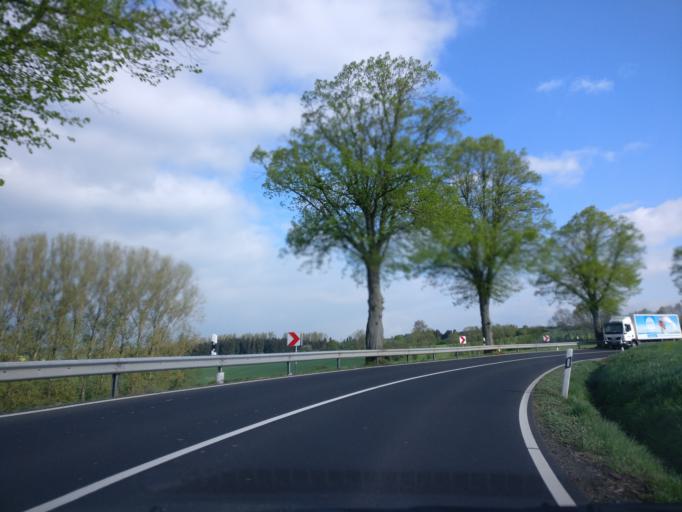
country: DE
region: Lower Saxony
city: Scheden
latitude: 51.4658
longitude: 9.7198
